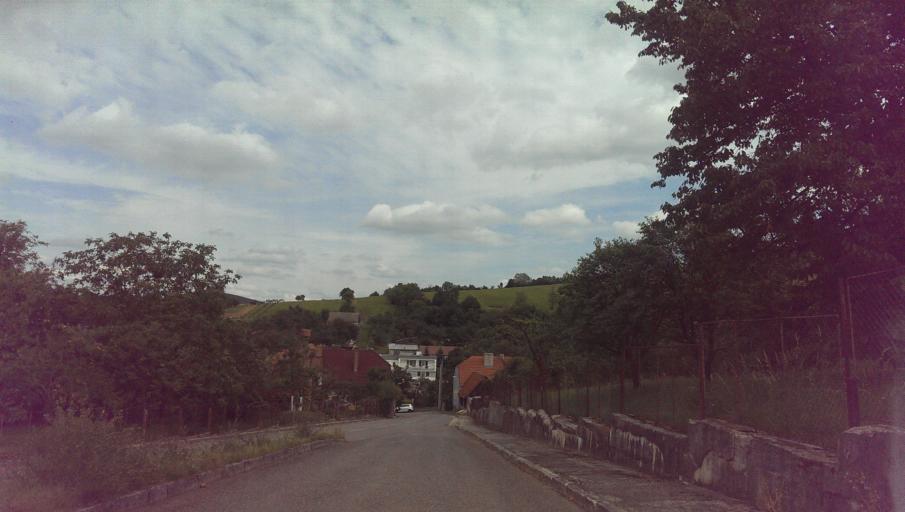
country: CZ
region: South Moravian
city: Velka nad Velickou
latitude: 48.8590
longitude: 17.5934
